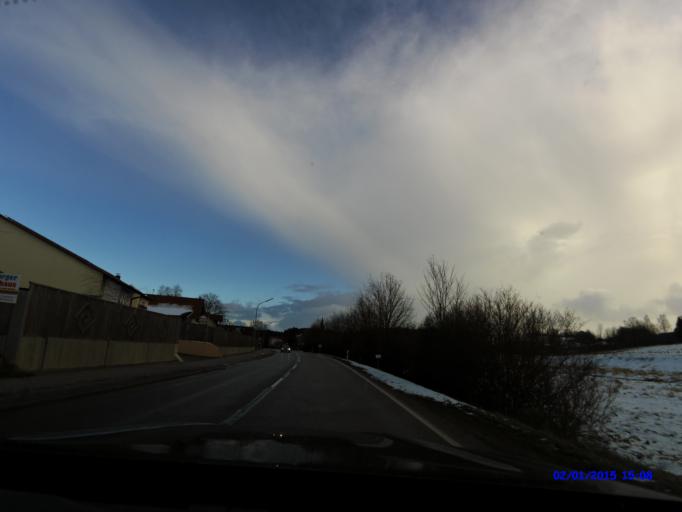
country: DE
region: Bavaria
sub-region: Upper Bavaria
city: Rudelzhausen
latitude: 48.6295
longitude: 11.7407
